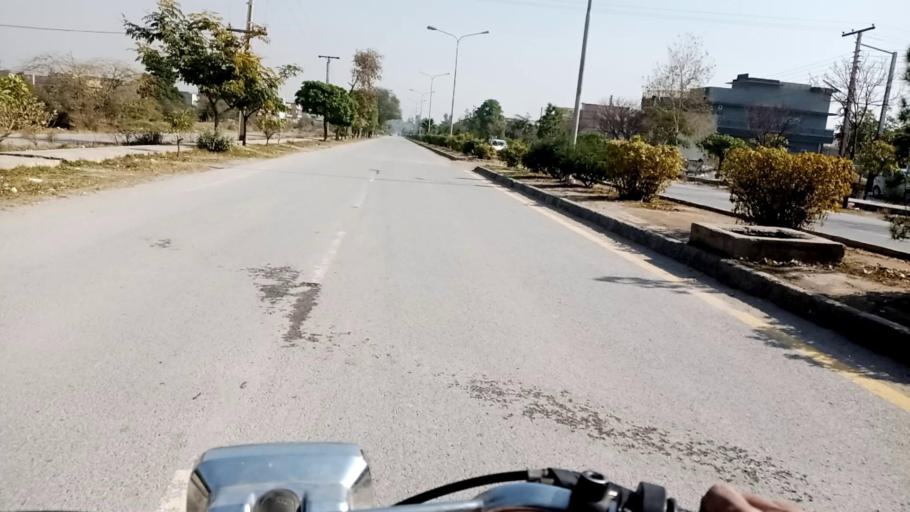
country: PK
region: Khyber Pakhtunkhwa
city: Peshawar
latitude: 33.9630
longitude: 71.4183
